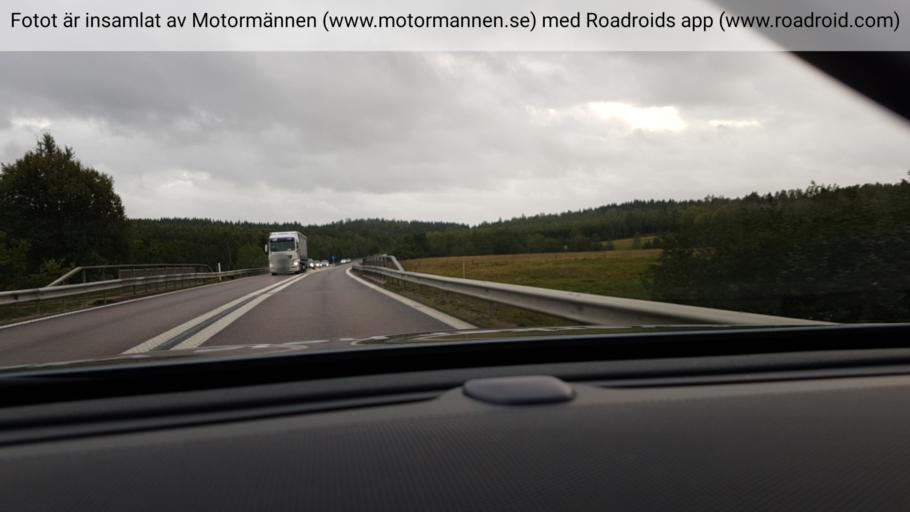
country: SE
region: Vaestra Goetaland
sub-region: Uddevalla Kommun
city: Uddevalla
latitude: 58.3312
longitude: 11.9745
